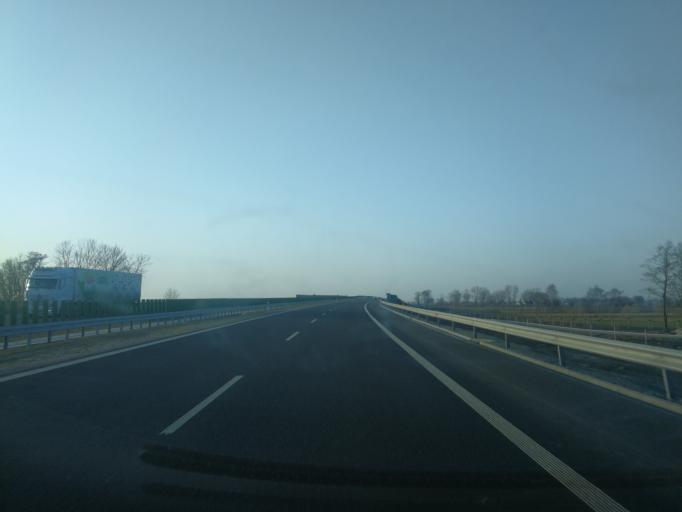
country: PL
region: Pomeranian Voivodeship
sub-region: Powiat nowodworski
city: Nowy Dwor Gdanski
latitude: 54.1782
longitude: 19.1853
